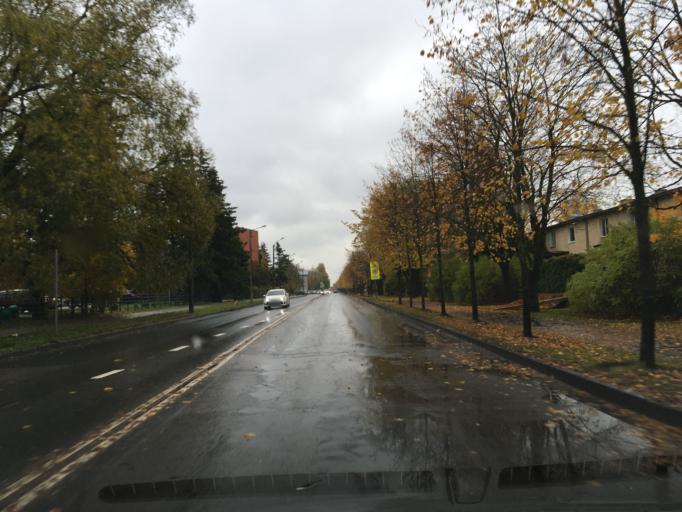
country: EE
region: Paernumaa
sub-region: Paernu linn
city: Parnu
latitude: 58.3750
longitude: 24.5293
